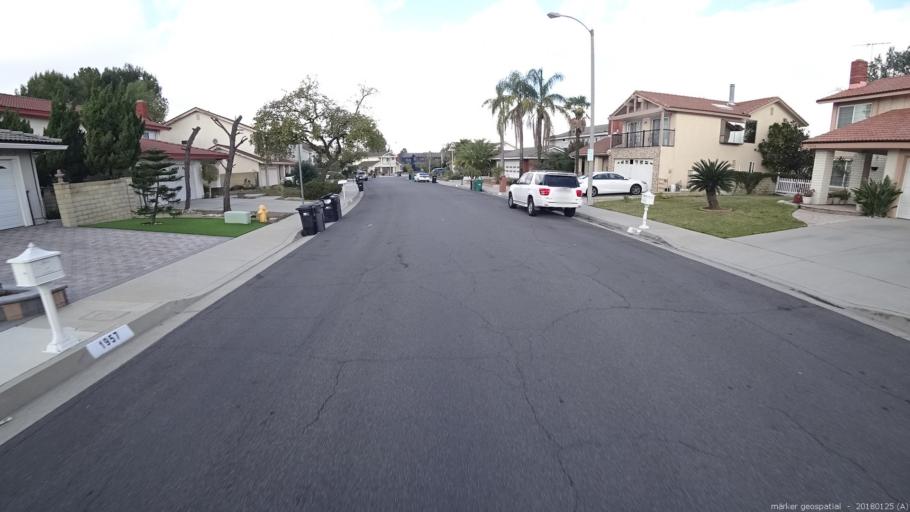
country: US
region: California
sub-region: Los Angeles County
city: Walnut
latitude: 33.9860
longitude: -117.8387
